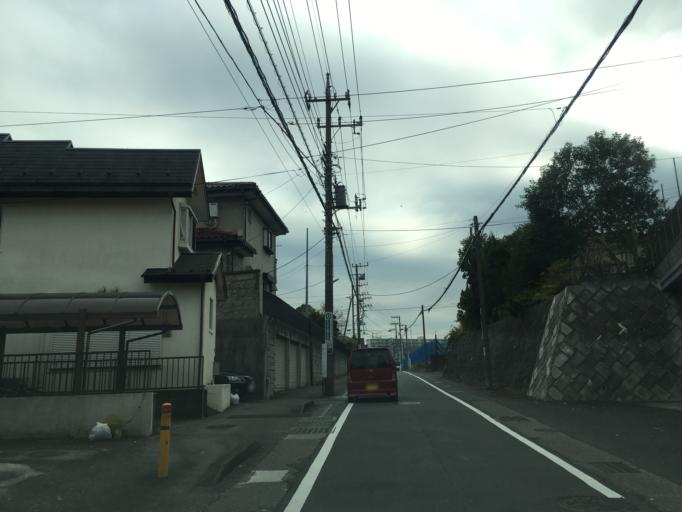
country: JP
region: Kanagawa
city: Minami-rinkan
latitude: 35.5087
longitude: 139.4638
